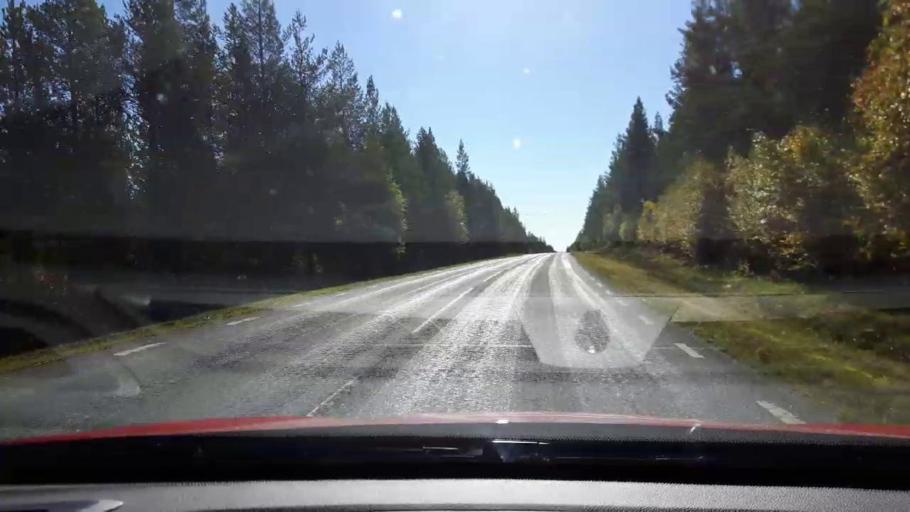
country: SE
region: Jaemtland
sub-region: Harjedalens Kommun
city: Sveg
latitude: 62.3511
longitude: 14.0300
